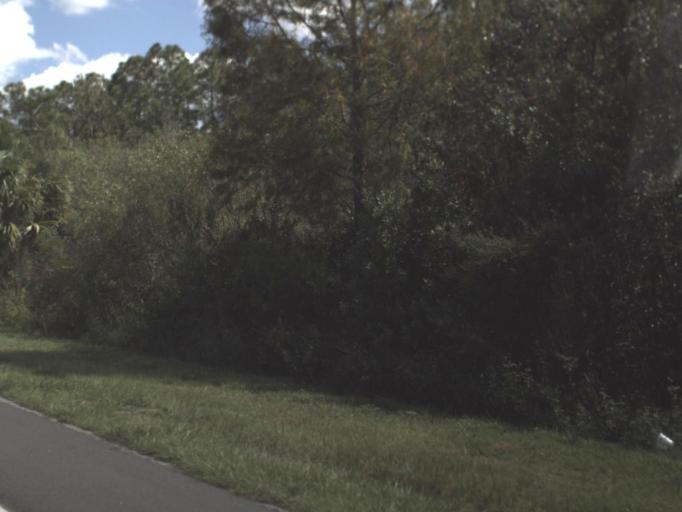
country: US
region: Florida
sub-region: Collier County
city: Marco
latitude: 25.8775
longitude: -81.2366
